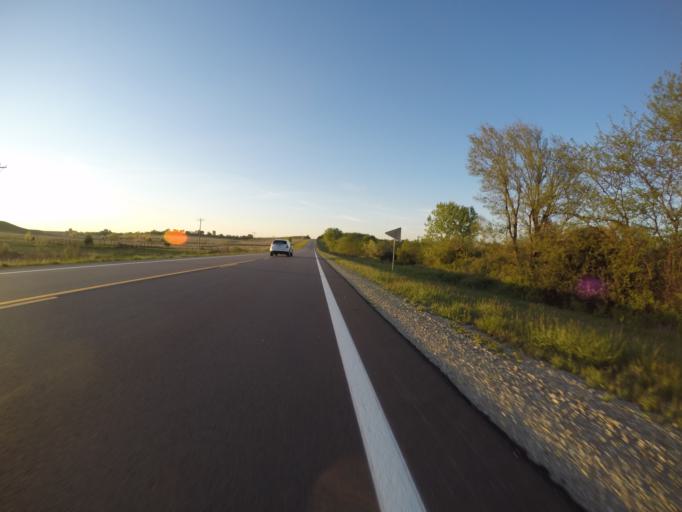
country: US
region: Kansas
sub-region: Pottawatomie County
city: Westmoreland
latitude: 39.4002
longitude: -96.5199
